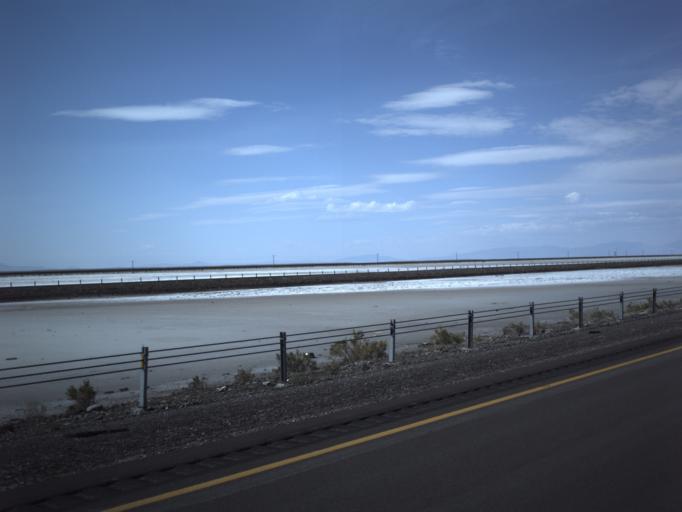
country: US
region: Utah
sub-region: Tooele County
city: Wendover
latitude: 40.7299
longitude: -113.4203
